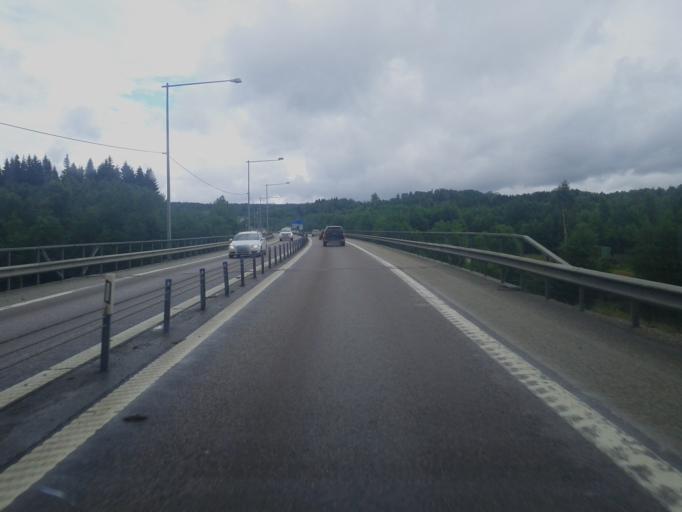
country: SE
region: Vaesternorrland
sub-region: Timra Kommun
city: Soraker
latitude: 62.5202
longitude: 17.4680
